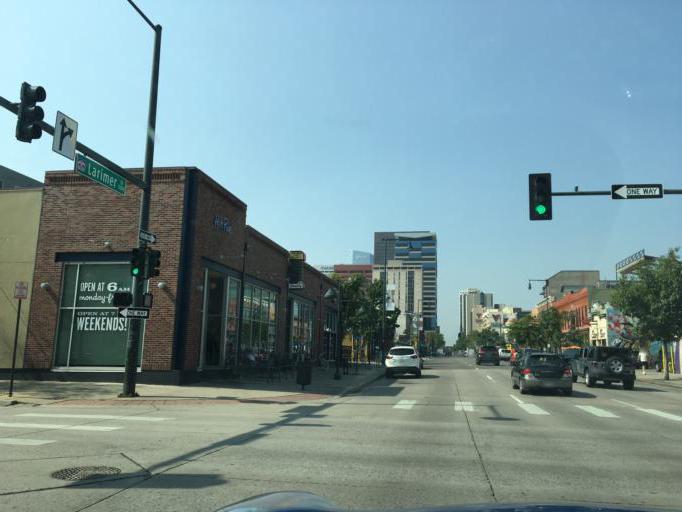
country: US
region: Colorado
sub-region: Denver County
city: Denver
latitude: 39.7548
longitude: -104.9901
